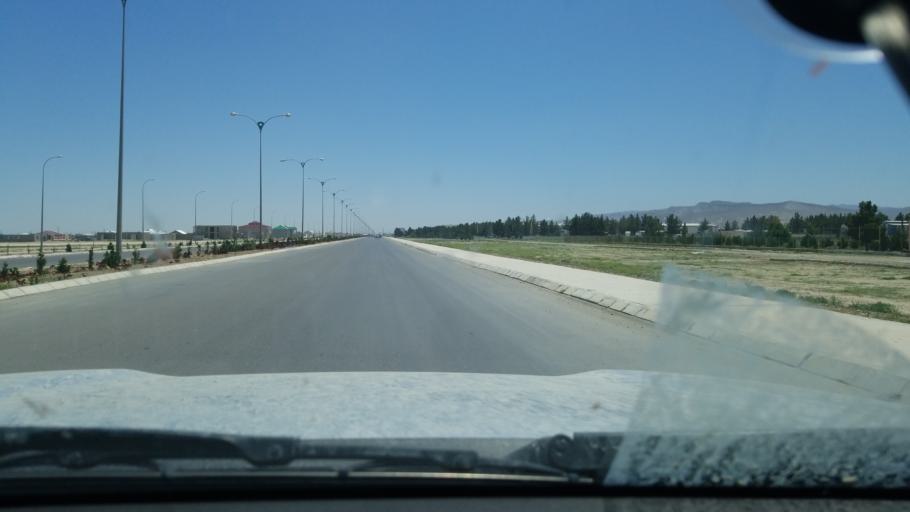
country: TM
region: Balkan
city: Serdar
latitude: 39.0041
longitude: 56.2543
